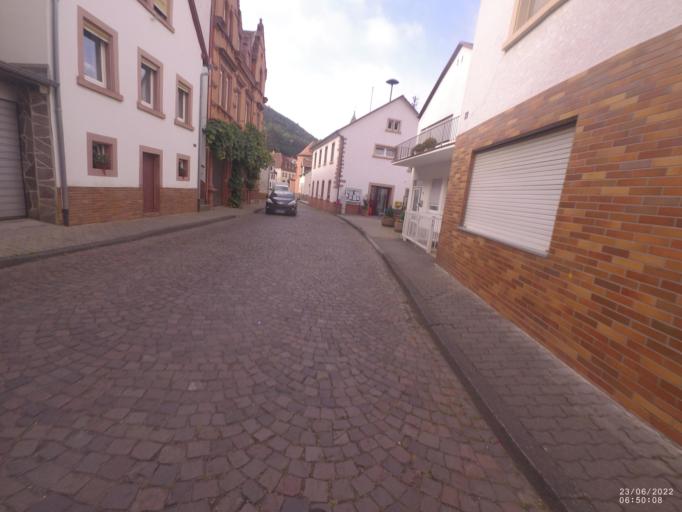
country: DE
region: Rheinland-Pfalz
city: Lindenberg
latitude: 49.3822
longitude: 8.0977
